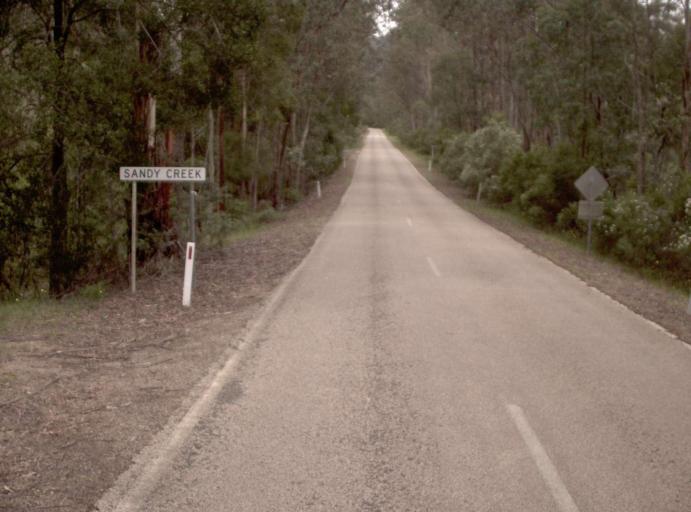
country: AU
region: Victoria
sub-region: East Gippsland
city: Bairnsdale
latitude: -37.6323
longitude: 147.2214
